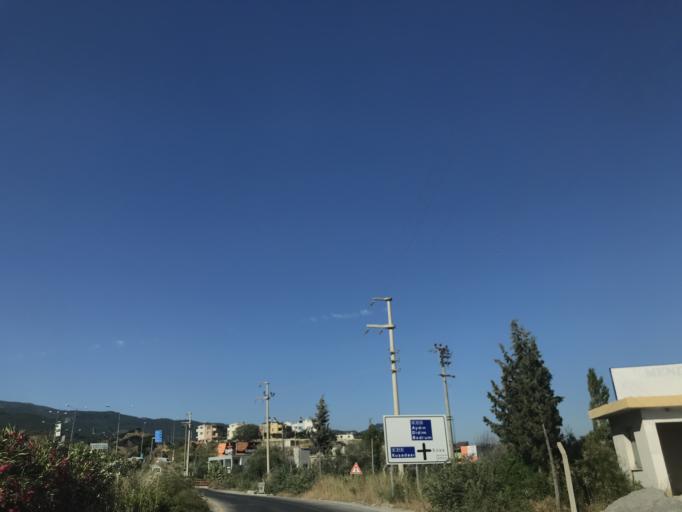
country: TR
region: Aydin
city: Soeke
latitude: 37.7602
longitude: 27.3760
